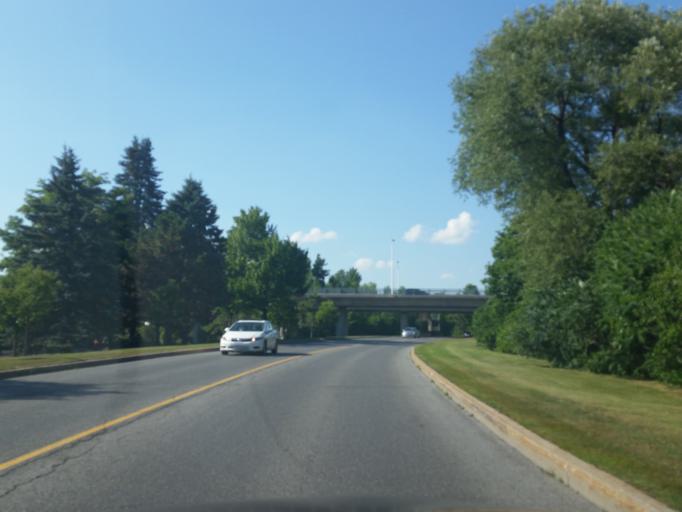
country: CA
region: Ontario
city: Ottawa
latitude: 45.3743
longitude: -75.7015
